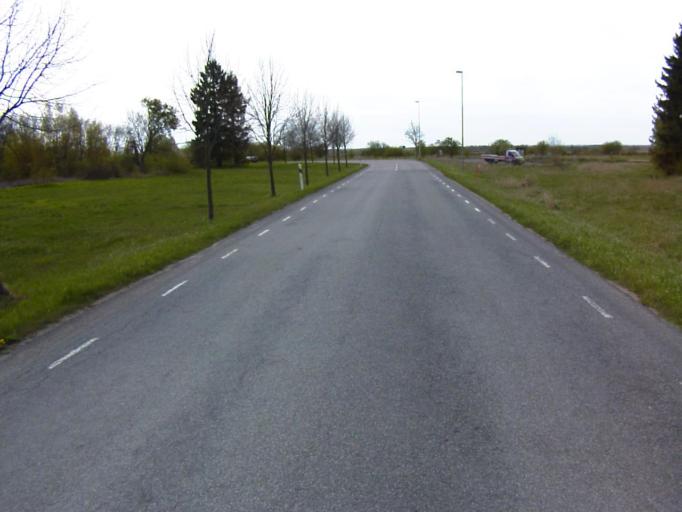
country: SE
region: Skane
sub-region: Kristianstads Kommun
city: Kristianstad
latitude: 56.0466
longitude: 14.1433
